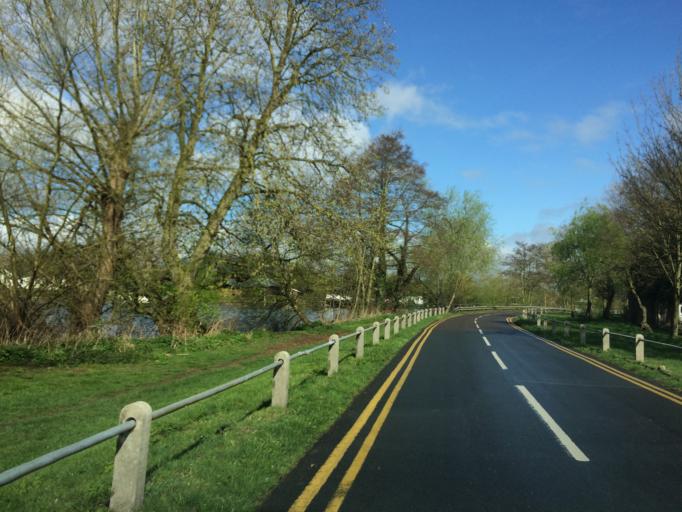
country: GB
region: England
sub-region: Surrey
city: Chertsey
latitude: 51.3998
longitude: -0.4911
